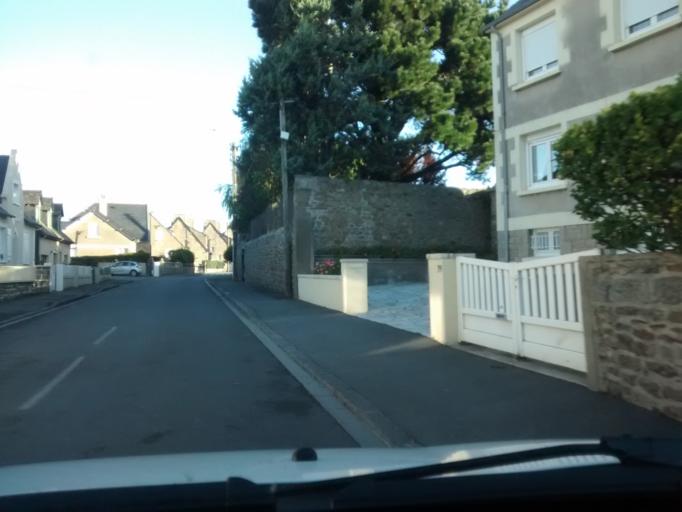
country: FR
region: Brittany
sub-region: Departement d'Ille-et-Vilaine
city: Saint-Malo
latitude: 48.6513
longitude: -1.9828
